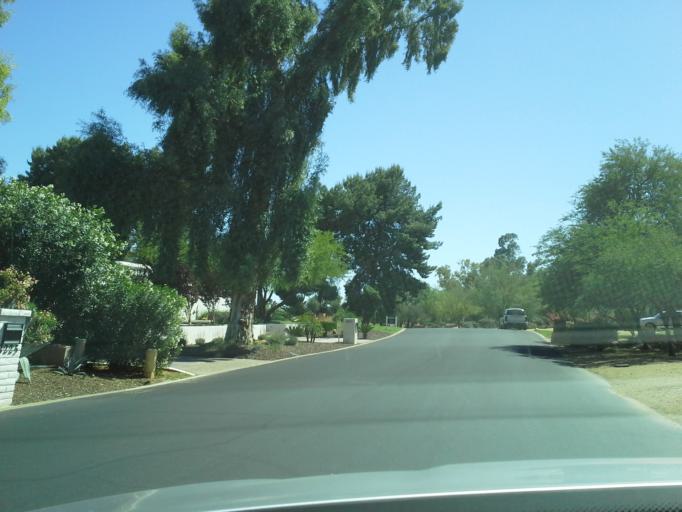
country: US
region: Arizona
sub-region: Maricopa County
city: Paradise Valley
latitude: 33.5568
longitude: -111.9279
